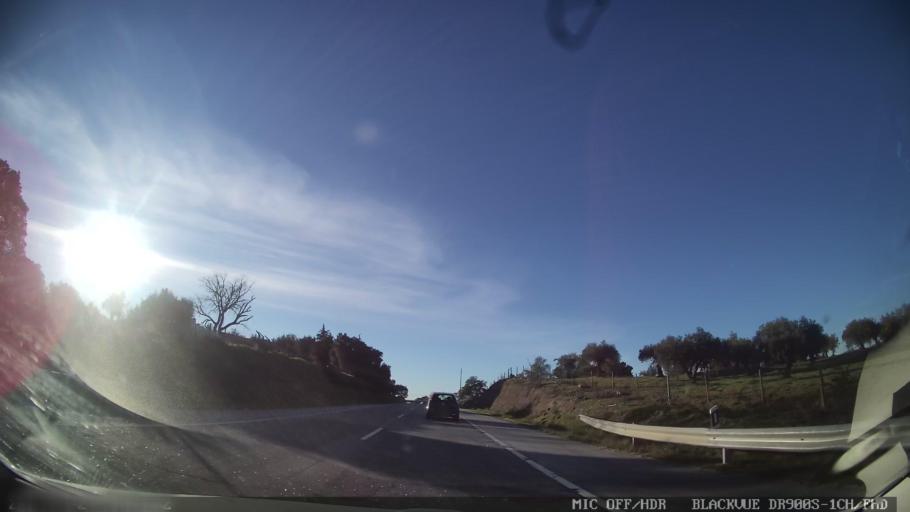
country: PT
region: Castelo Branco
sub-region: Castelo Branco
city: Castelo Branco
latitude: 39.8448
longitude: -7.4892
